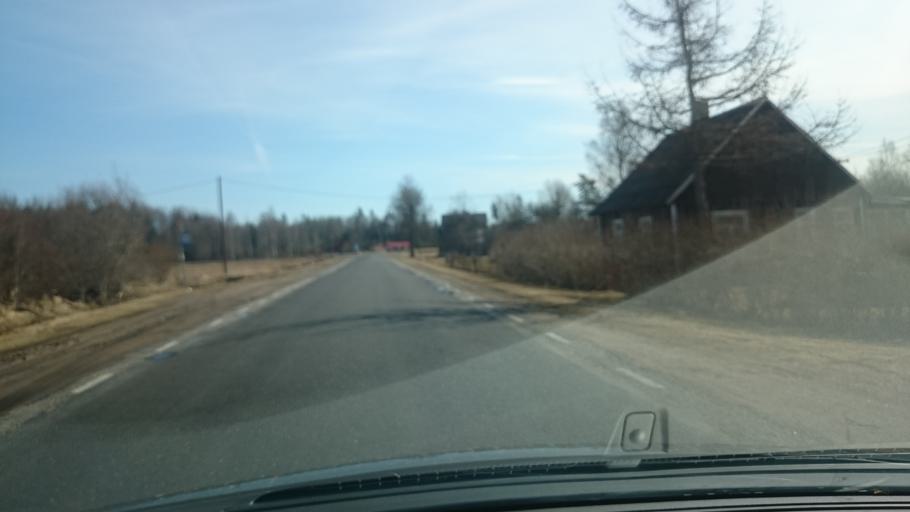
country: EE
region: Paernumaa
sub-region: Tootsi vald
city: Tootsi
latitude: 58.6461
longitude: 24.8656
